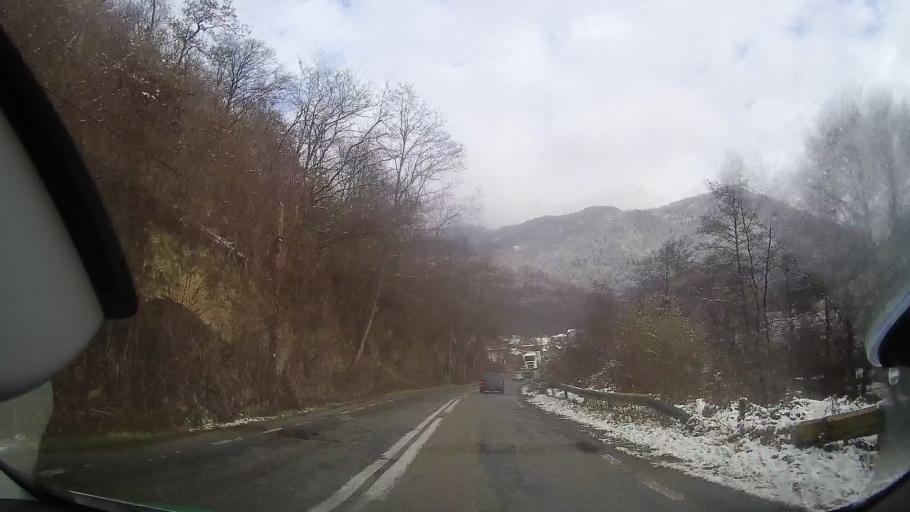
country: RO
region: Alba
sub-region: Oras Baia de Aries
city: Baia de Aries
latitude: 46.4043
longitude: 23.3247
